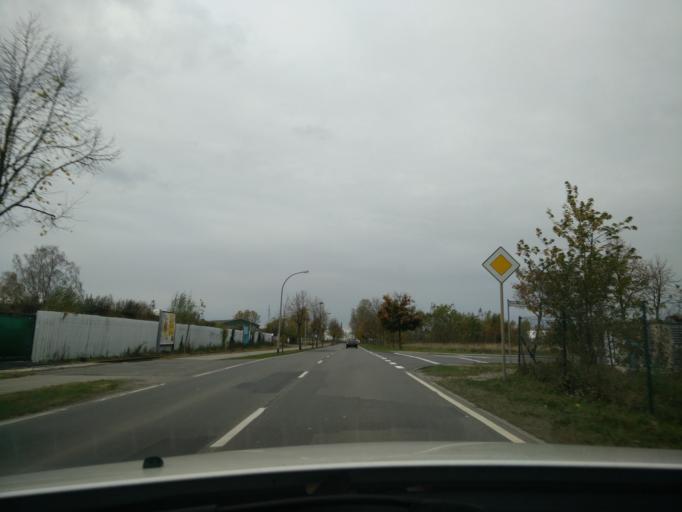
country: DE
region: Brandenburg
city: Velten
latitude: 52.6800
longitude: 13.1956
